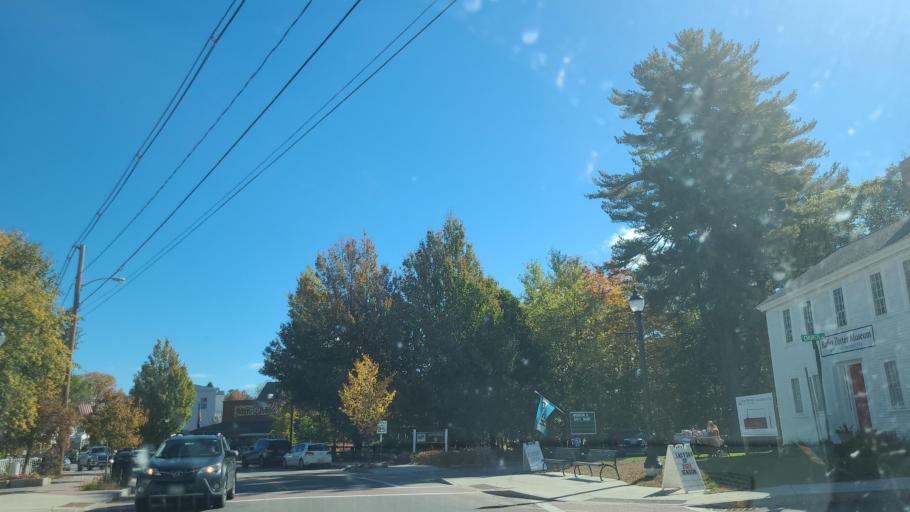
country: US
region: Maine
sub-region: Cumberland County
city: Bridgton
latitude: 44.0545
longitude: -70.7096
